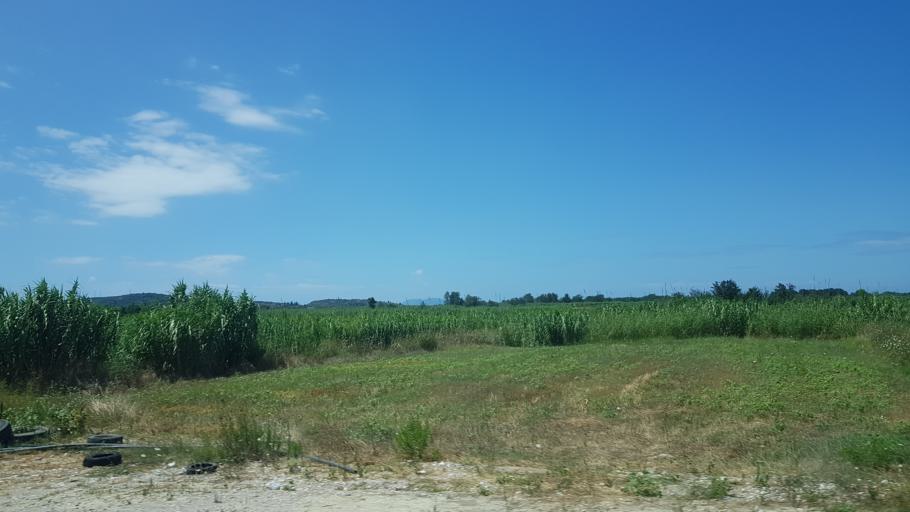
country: AL
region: Fier
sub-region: Rrethi i Fierit
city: Frakulla e Madhe
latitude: 40.6228
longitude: 19.5153
